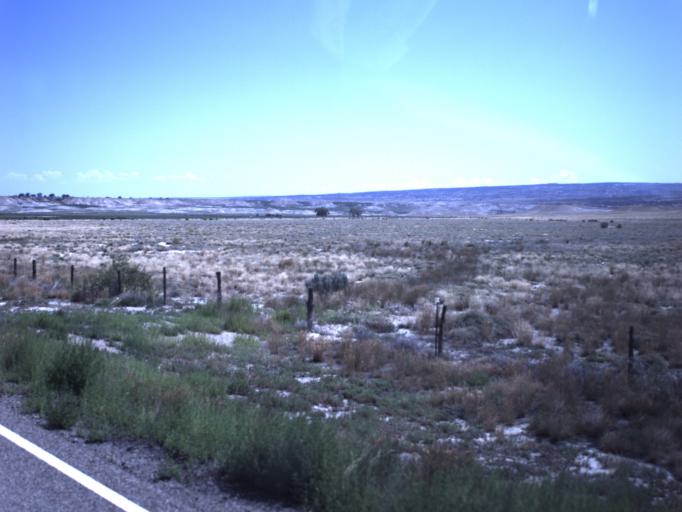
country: US
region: Utah
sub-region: Emery County
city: Ferron
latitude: 38.8547
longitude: -111.3054
